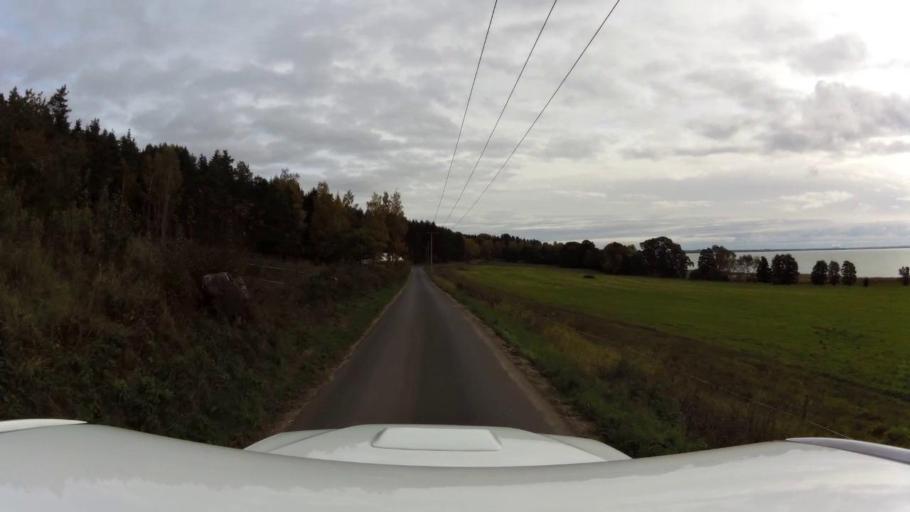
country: SE
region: OEstergoetland
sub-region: Linkopings Kommun
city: Berg
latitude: 58.5115
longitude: 15.5543
